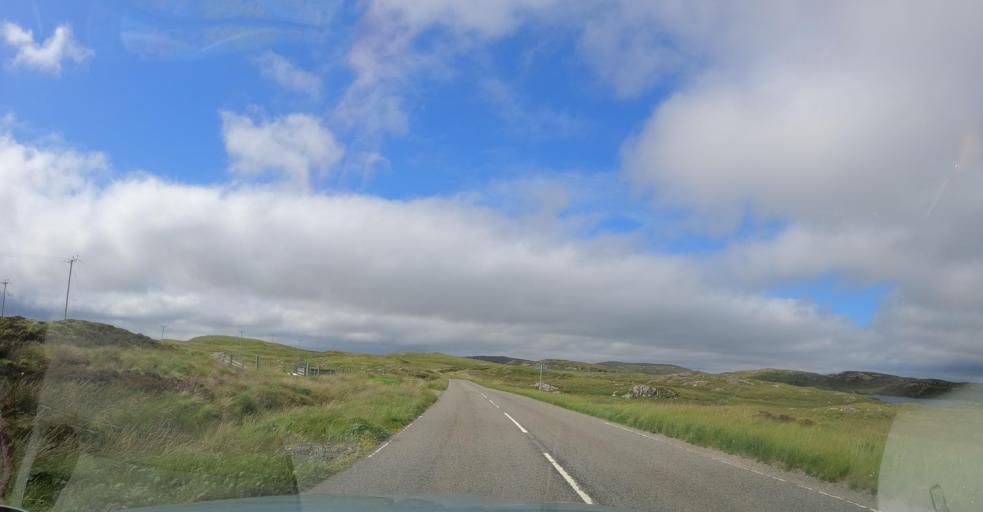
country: GB
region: Scotland
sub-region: Eilean Siar
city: Stornoway
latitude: 58.1118
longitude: -6.5104
